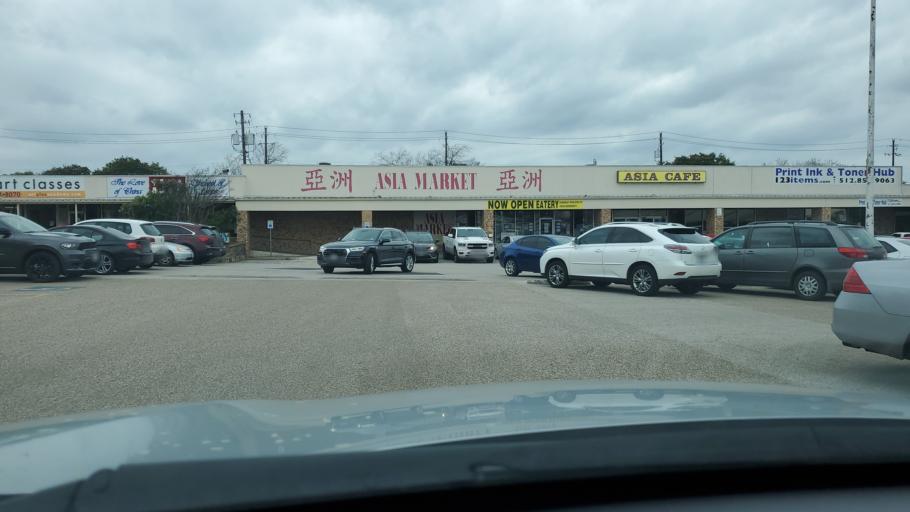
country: US
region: Texas
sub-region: Williamson County
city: Jollyville
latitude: 30.4325
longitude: -97.7708
